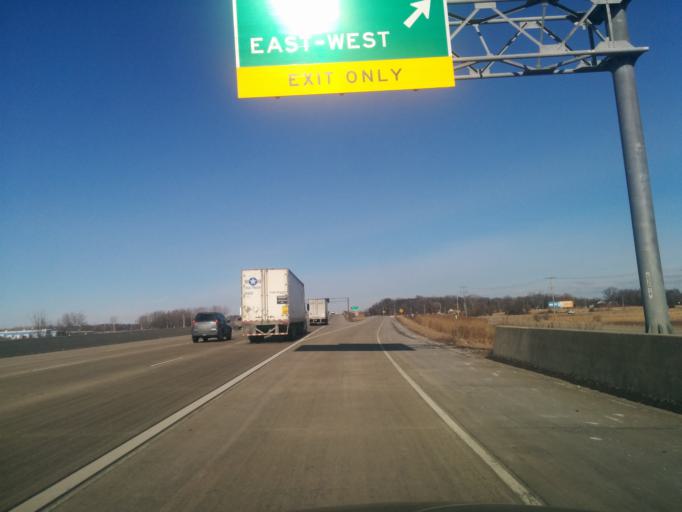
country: US
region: Wisconsin
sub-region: Kenosha County
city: Pleasant Prairie
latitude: 42.5390
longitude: -87.9520
